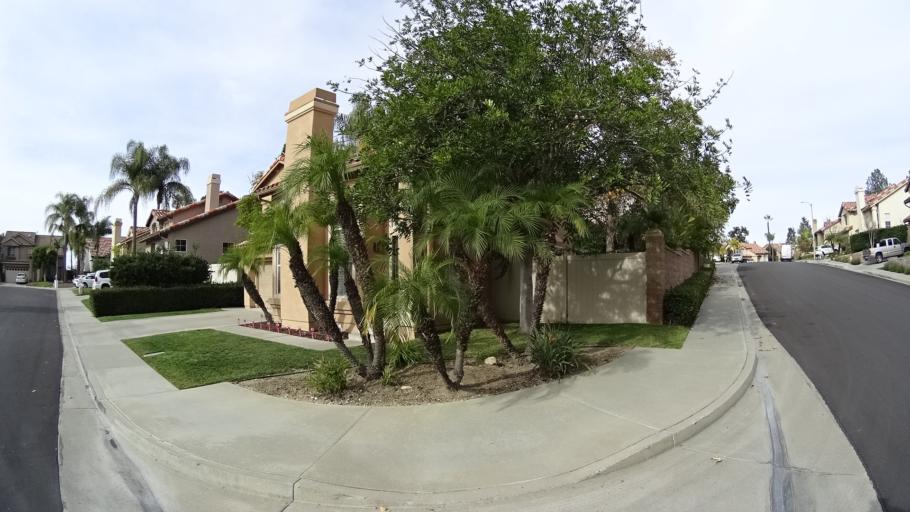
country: US
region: California
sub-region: Orange County
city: Laguna Woods
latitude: 33.6034
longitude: -117.7359
